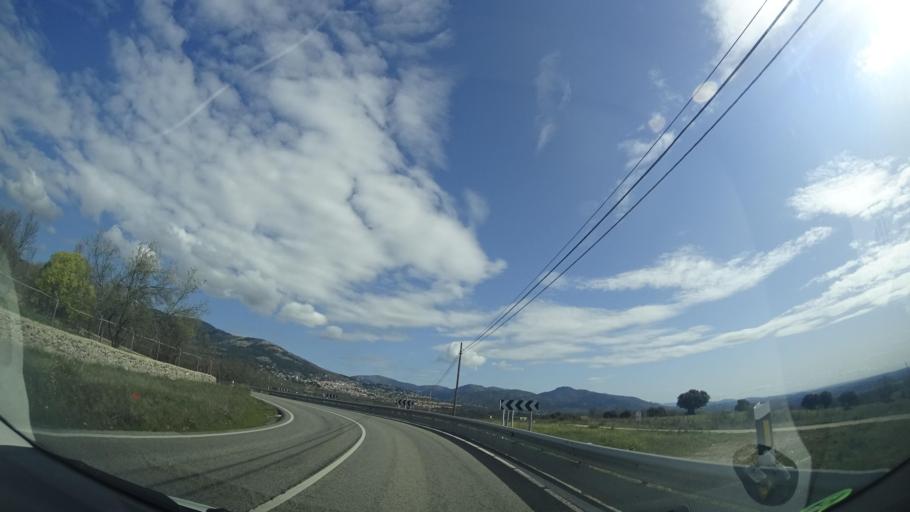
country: ES
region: Madrid
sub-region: Provincia de Madrid
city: Miraflores de la Sierra
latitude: 40.7847
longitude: -3.7726
